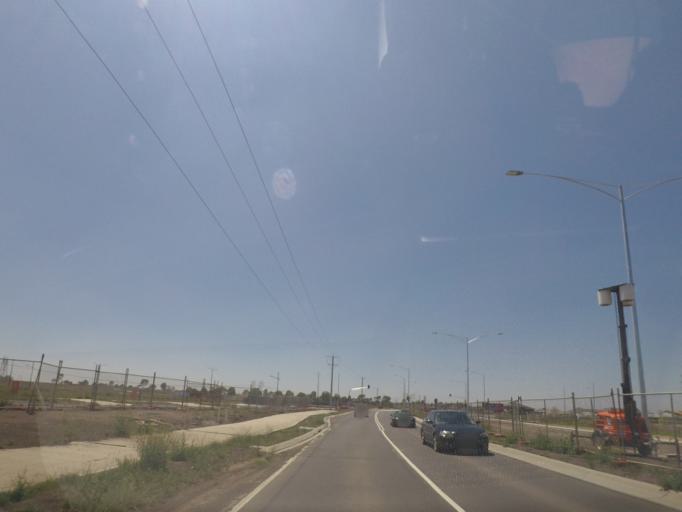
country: AU
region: Victoria
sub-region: Whittlesea
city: Epping
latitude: -37.6057
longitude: 145.0044
